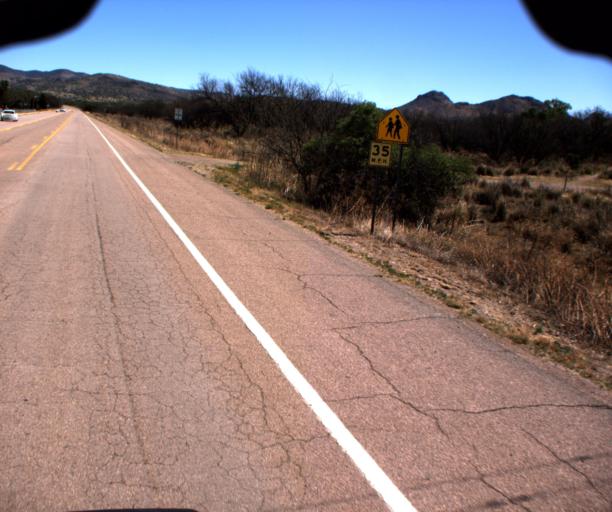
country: US
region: Arizona
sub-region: Santa Cruz County
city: Rio Rico
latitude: 31.5438
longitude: -110.7481
